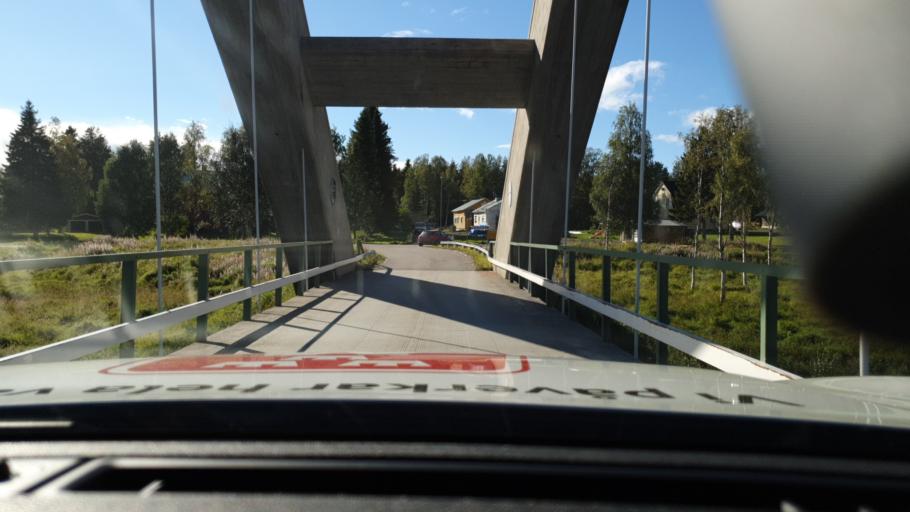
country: SE
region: Norrbotten
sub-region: Pajala Kommun
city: Pajala
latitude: 67.1677
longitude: 22.6112
